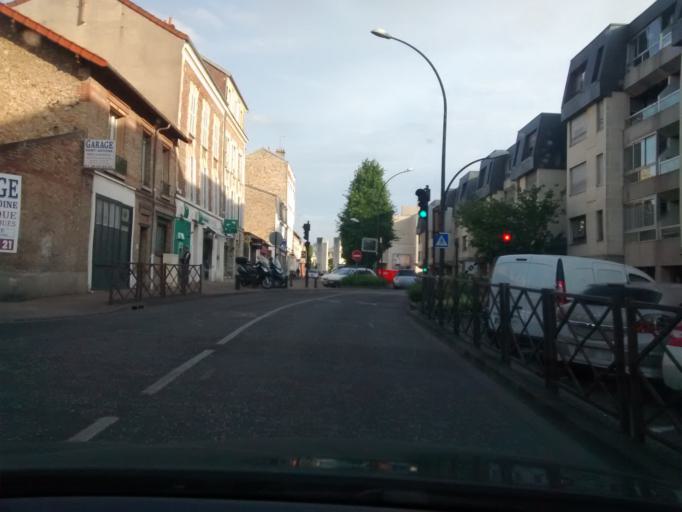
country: FR
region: Ile-de-France
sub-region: Departement des Yvelines
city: Le Chesnay
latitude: 48.8170
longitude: 2.1279
